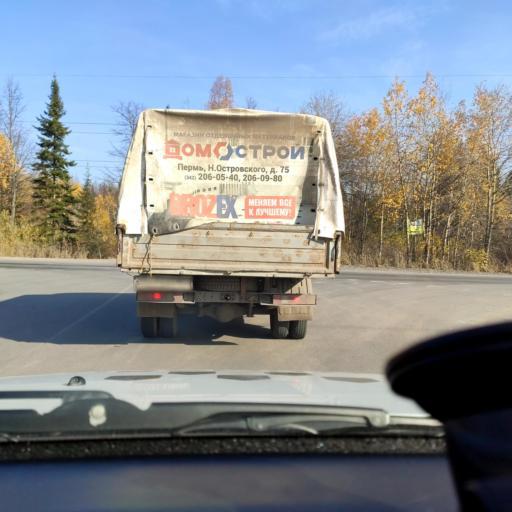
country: RU
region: Perm
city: Ferma
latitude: 57.9653
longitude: 56.3503
